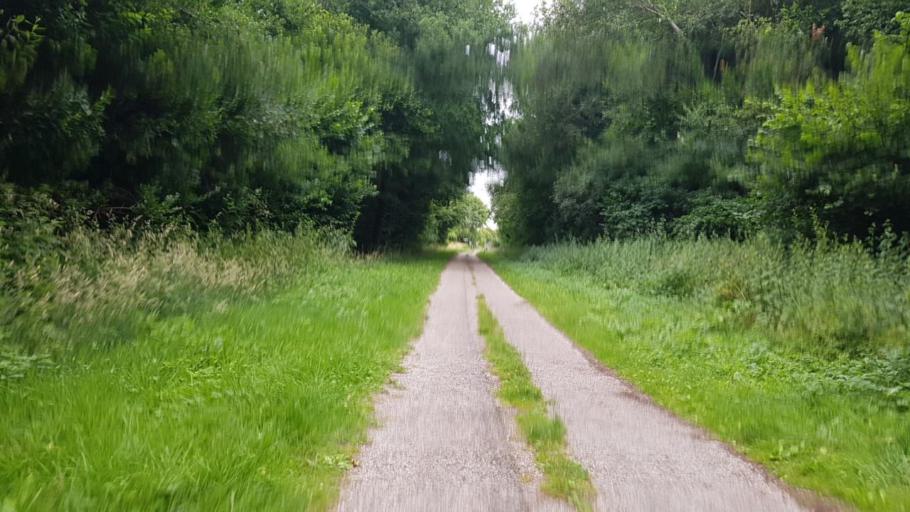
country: FR
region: Picardie
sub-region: Departement de l'Aisne
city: Origny-en-Thierache
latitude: 49.9265
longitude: 4.0391
